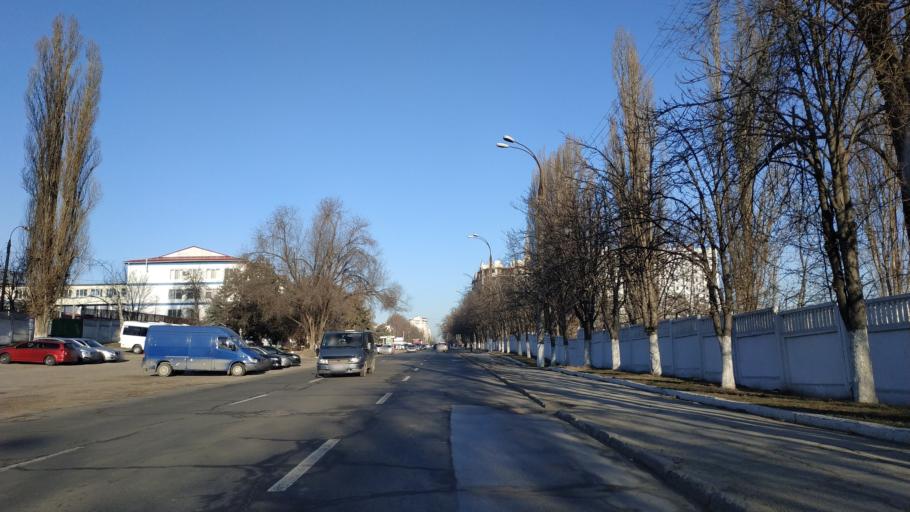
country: MD
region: Chisinau
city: Chisinau
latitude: 46.9807
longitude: 28.8818
